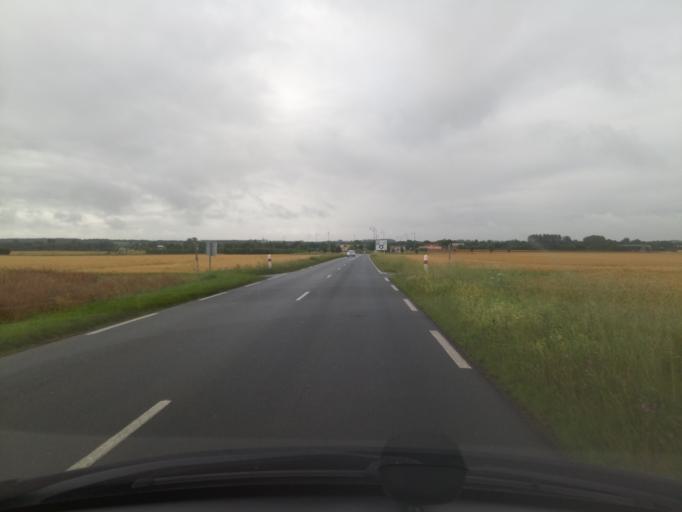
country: FR
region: Poitou-Charentes
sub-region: Departement de la Charente-Maritime
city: Saint-Jean-de-Liversay
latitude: 46.1979
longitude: -0.8699
